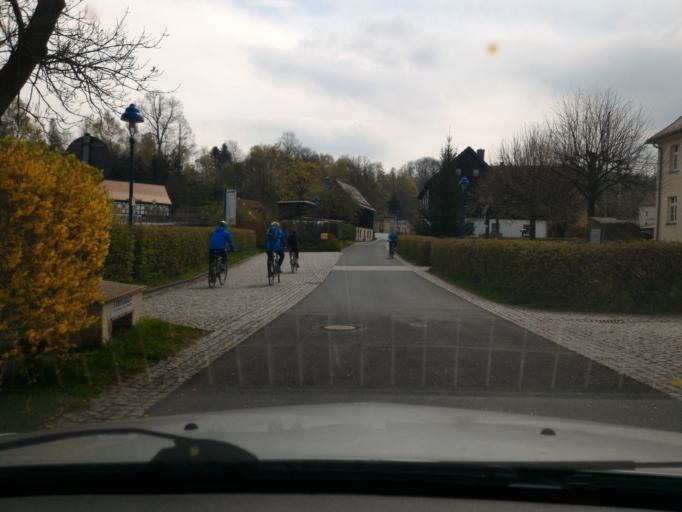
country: DE
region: Saxony
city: Hainewalde
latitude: 50.9080
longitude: 14.7010
